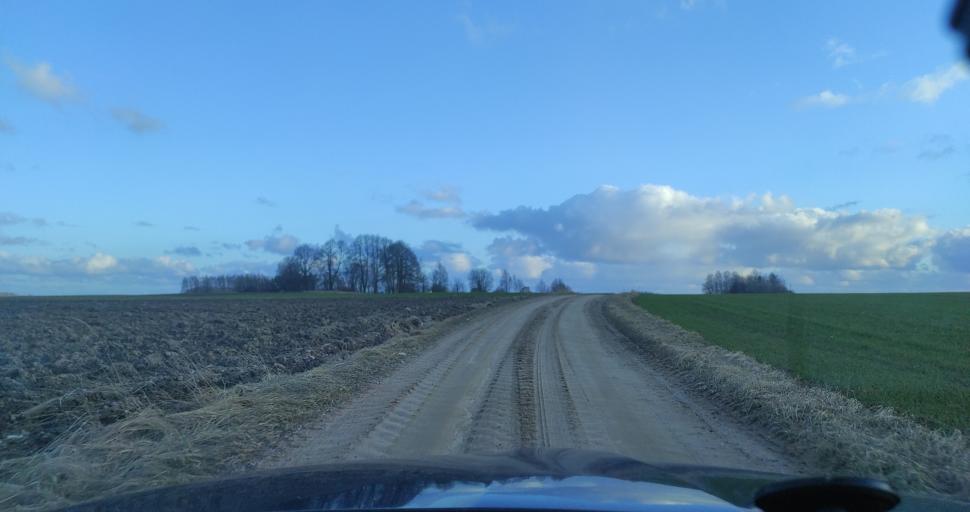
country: LV
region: Aizpute
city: Aizpute
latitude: 56.8608
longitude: 21.7606
